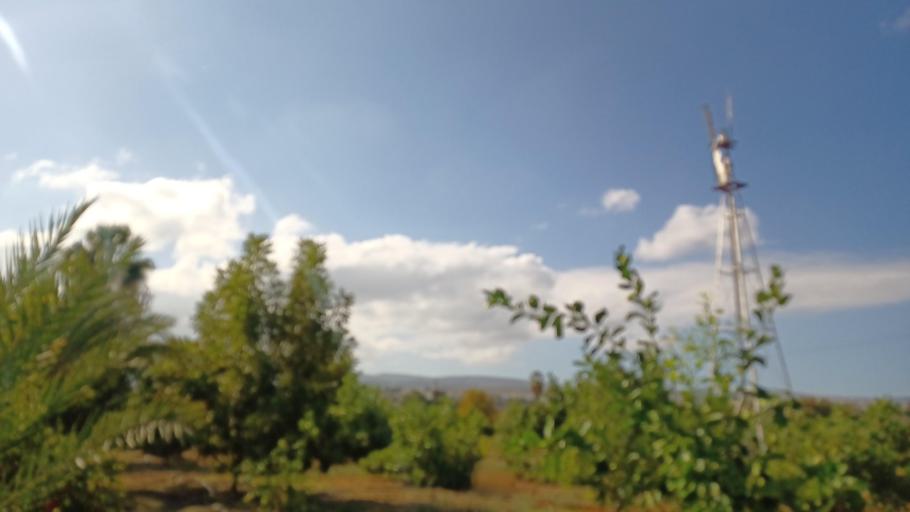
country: CY
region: Pafos
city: Polis
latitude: 35.0358
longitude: 32.4212
